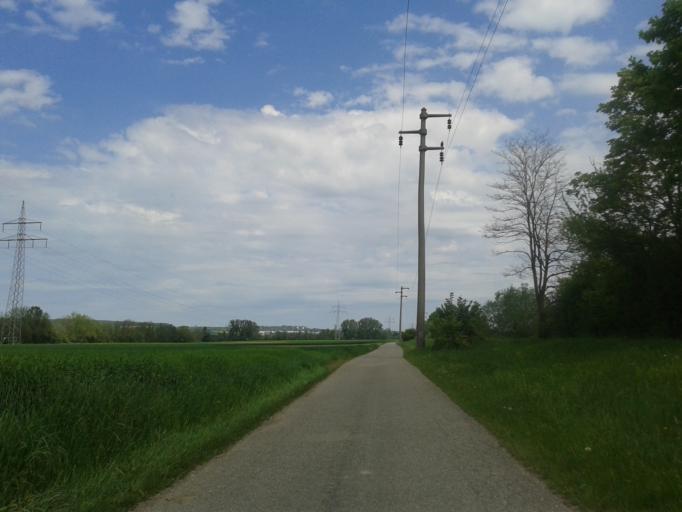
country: DE
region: Baden-Wuerttemberg
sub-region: Tuebingen Region
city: Erbach
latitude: 48.3340
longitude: 9.9308
